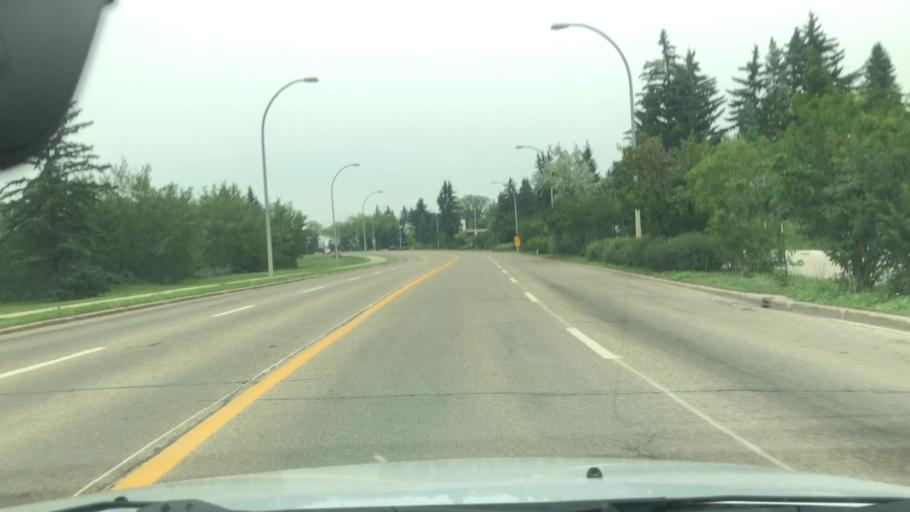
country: CA
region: Alberta
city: Edmonton
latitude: 53.5195
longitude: -113.5383
